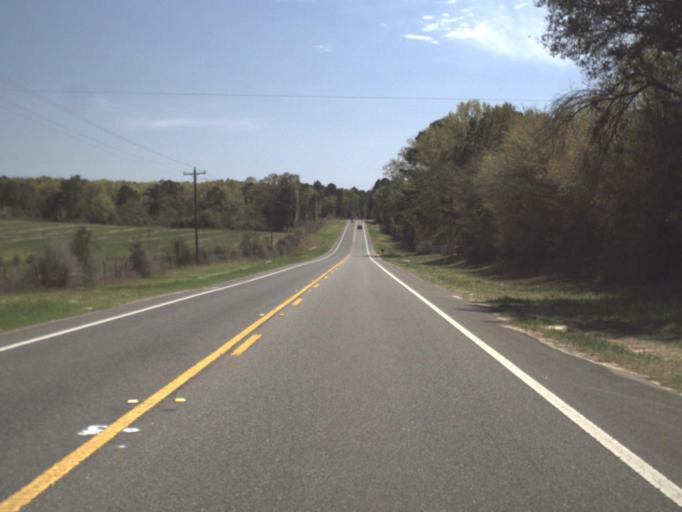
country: US
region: Alabama
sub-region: Geneva County
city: Geneva
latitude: 30.8682
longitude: -85.9457
